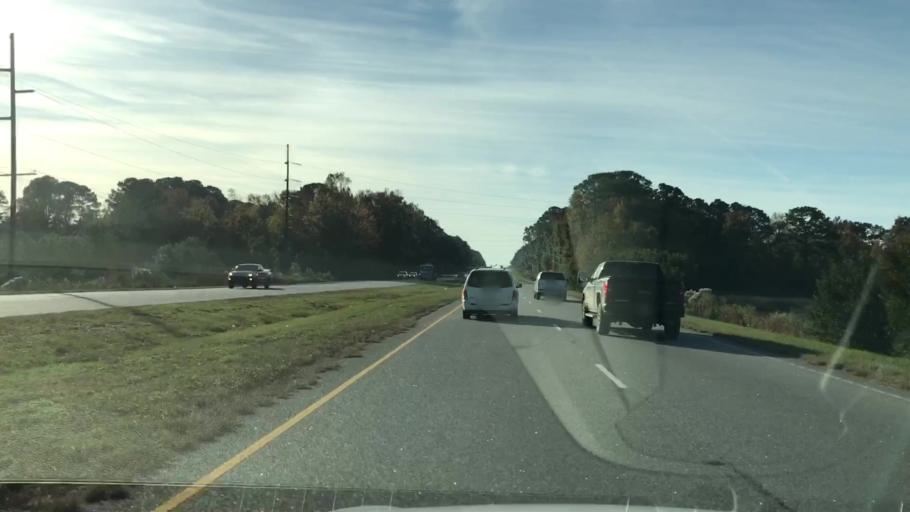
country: US
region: South Carolina
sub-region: Beaufort County
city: Laurel Bay
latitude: 32.5017
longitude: -80.7443
